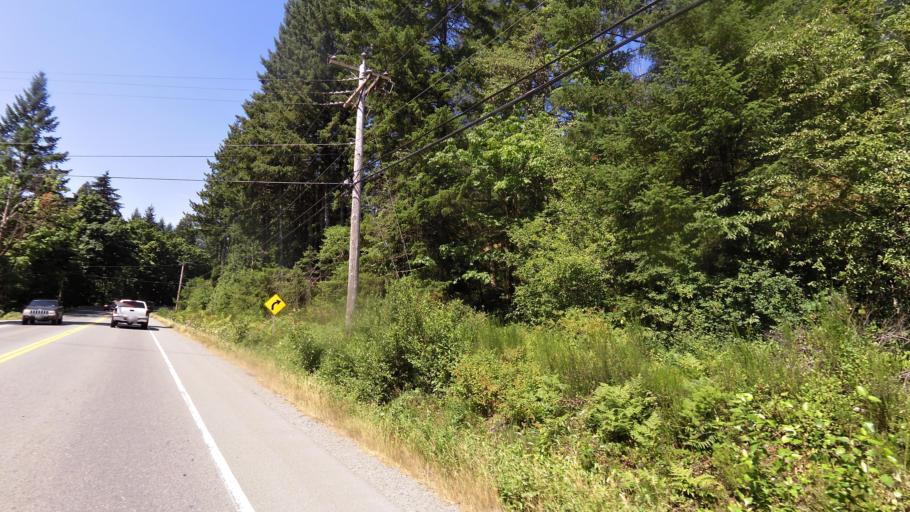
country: CA
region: British Columbia
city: Port Alberni
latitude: 49.2695
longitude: -124.8692
